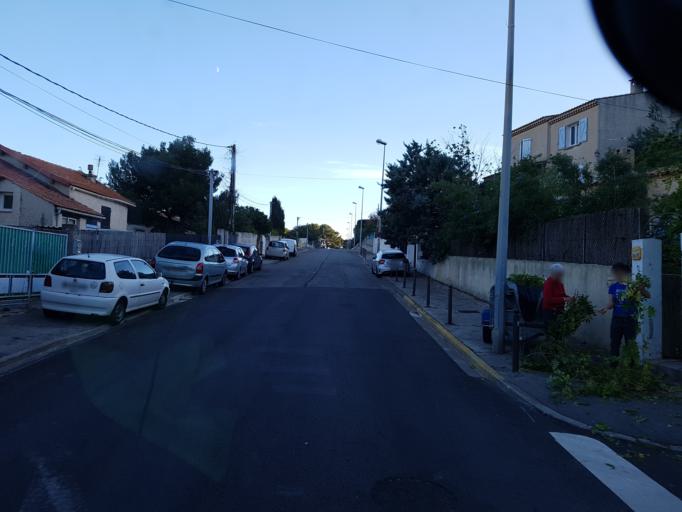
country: FR
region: Provence-Alpes-Cote d'Azur
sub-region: Departement des Bouches-du-Rhone
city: La Ciotat
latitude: 43.1748
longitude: 5.5979
